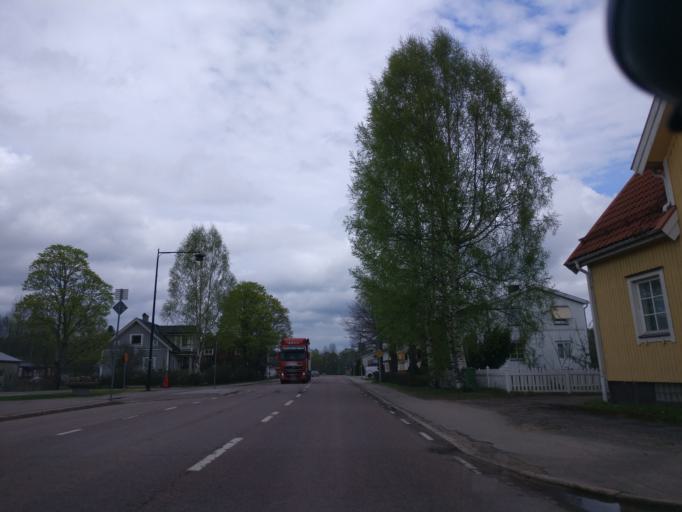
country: SE
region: Vaermland
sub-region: Hagfors Kommun
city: Ekshaerad
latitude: 60.1766
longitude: 13.4958
